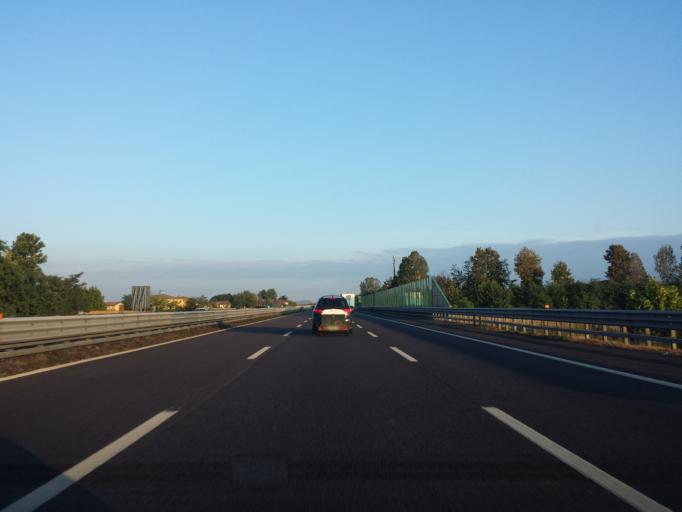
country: IT
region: Lombardy
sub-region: Provincia di Brescia
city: Buffalora-Bettole
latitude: 45.4934
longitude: 10.2804
